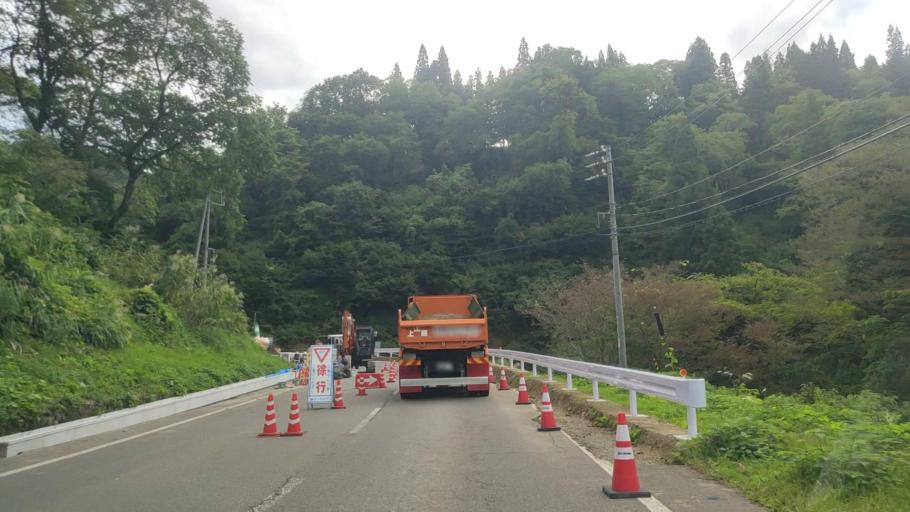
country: JP
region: Nagano
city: Iiyama
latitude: 36.9030
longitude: 138.3149
